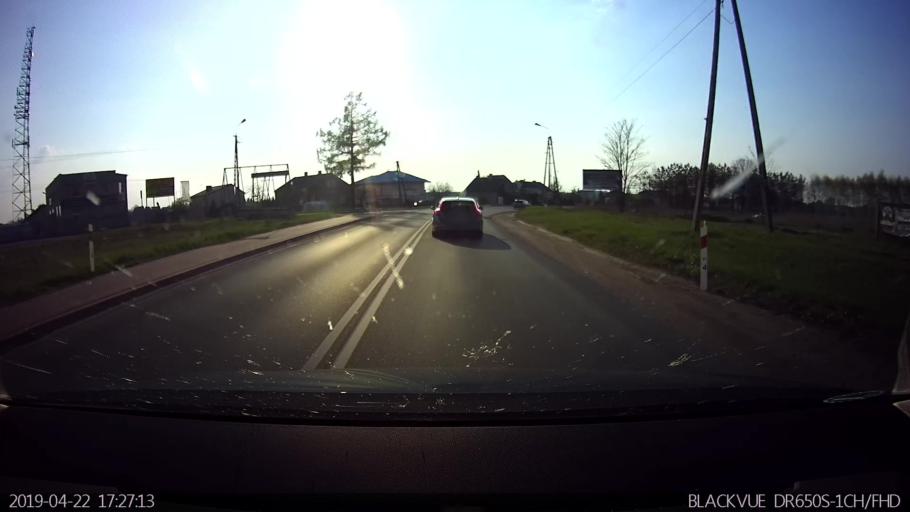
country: PL
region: Masovian Voivodeship
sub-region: Powiat sokolowski
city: Sokolow Podlaski
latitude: 52.3958
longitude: 22.2671
